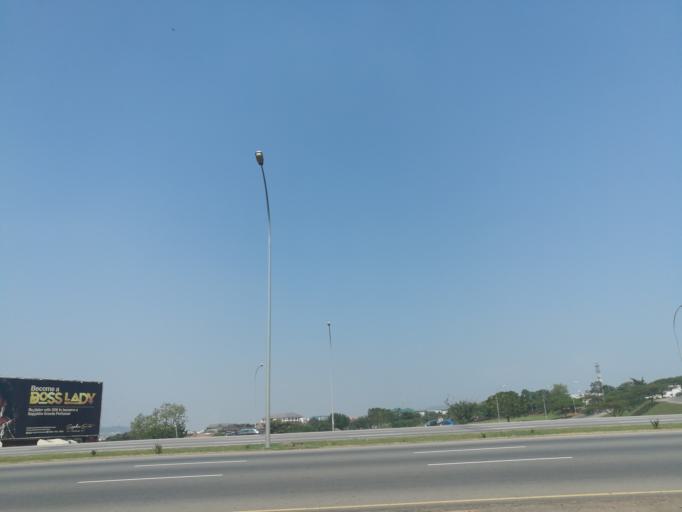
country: NG
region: Abuja Federal Capital Territory
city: Abuja
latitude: 9.0763
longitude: 7.4555
